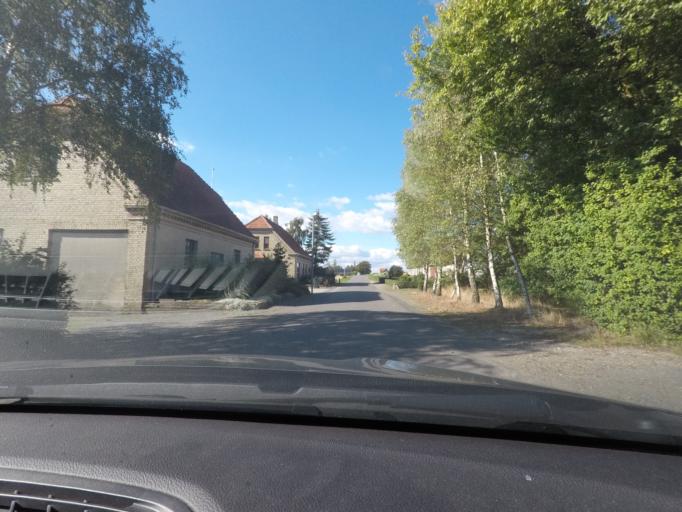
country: DK
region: Zealand
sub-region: Guldborgsund Kommune
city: Sakskobing
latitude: 54.9704
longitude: 11.5302
